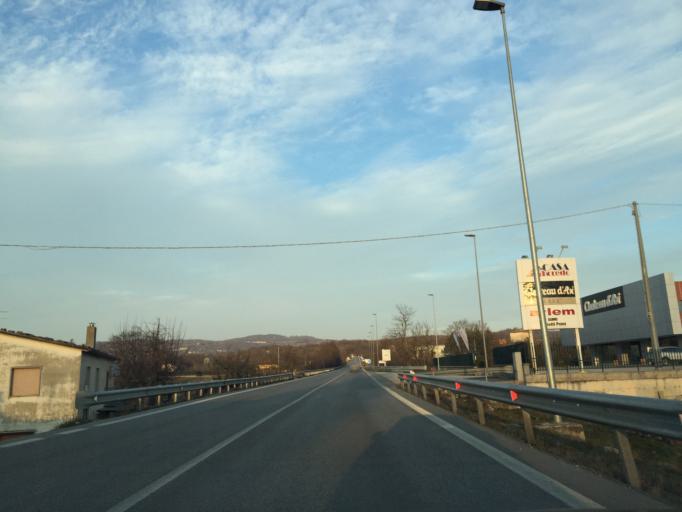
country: IT
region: Molise
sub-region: Provincia di Campobasso
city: Vinchiaturo
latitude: 41.4792
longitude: 14.5790
